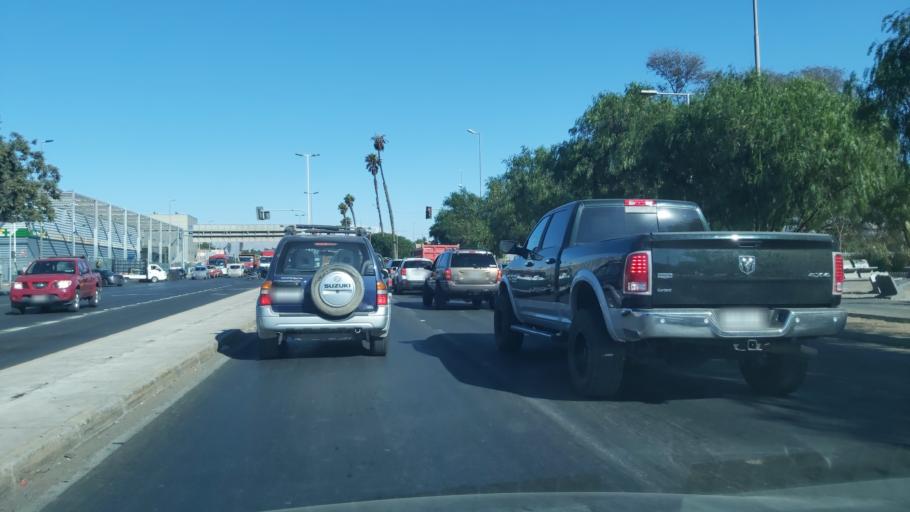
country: CL
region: Atacama
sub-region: Provincia de Copiapo
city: Copiapo
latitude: -27.3692
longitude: -70.3369
